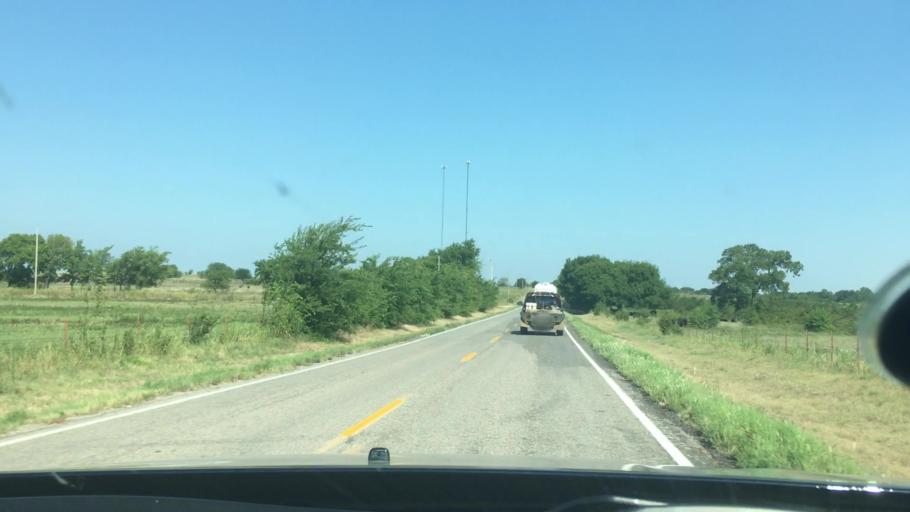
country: US
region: Oklahoma
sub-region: Johnston County
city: Tishomingo
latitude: 34.1893
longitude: -96.5296
